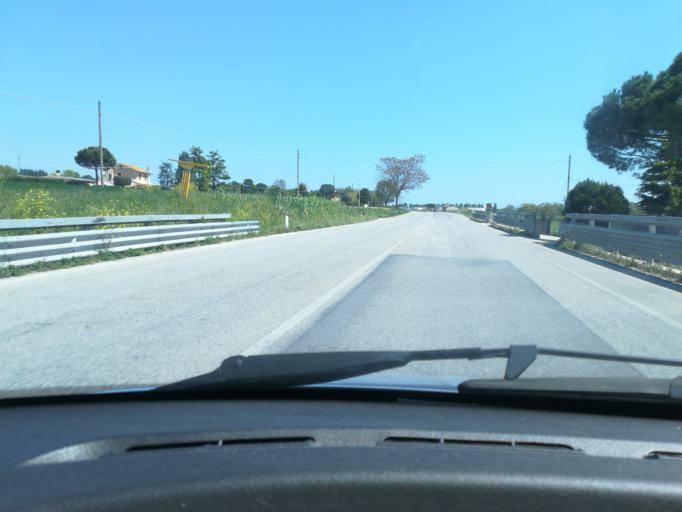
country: IT
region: The Marches
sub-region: Provincia di Ancona
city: Castelfidardo
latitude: 43.4466
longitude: 13.5687
